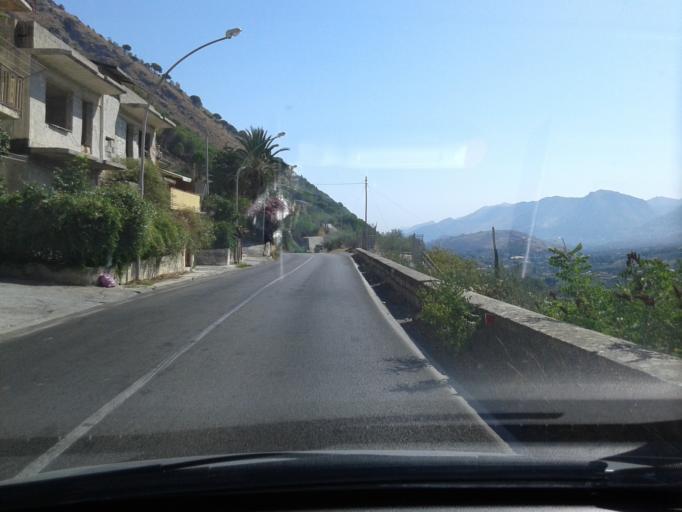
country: IT
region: Sicily
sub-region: Palermo
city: Pioppo
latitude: 38.0504
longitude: 13.2369
